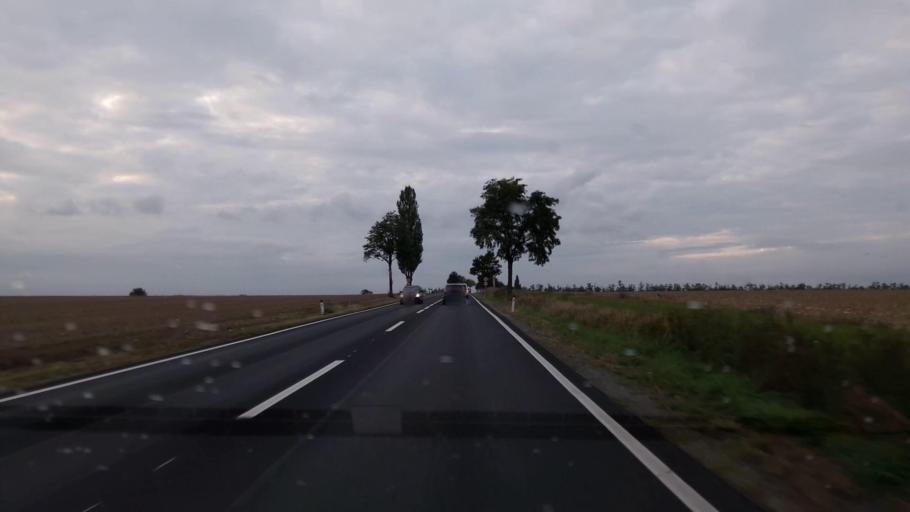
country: AT
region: Lower Austria
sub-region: Politischer Bezirk Wien-Umgebung
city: Schwadorf
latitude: 48.0880
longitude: 16.5567
